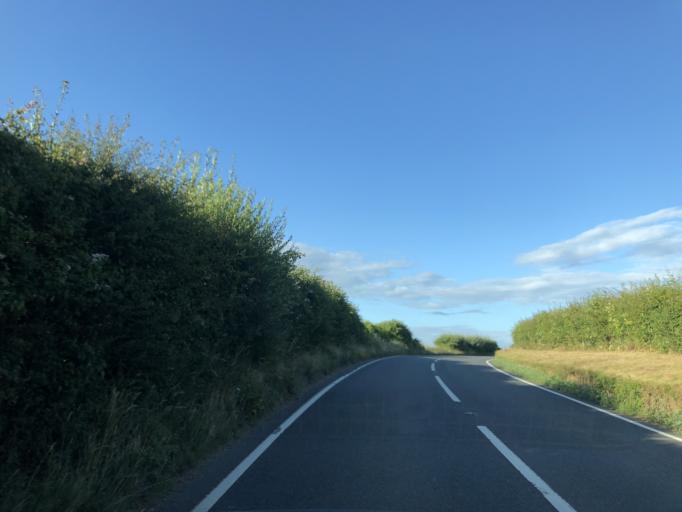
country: GB
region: England
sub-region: Isle of Wight
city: Shalfleet
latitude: 50.6741
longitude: -1.4286
